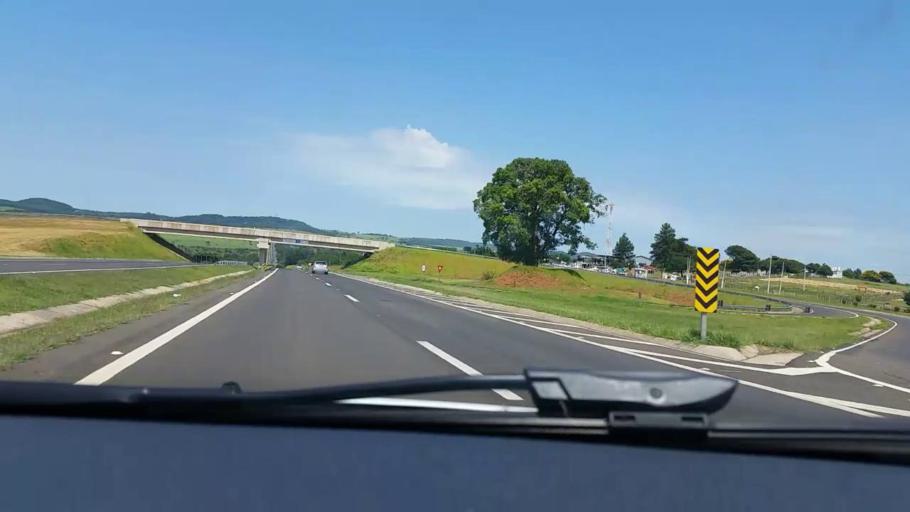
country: BR
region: Sao Paulo
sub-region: Bauru
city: Bauru
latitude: -22.3973
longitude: -49.0866
